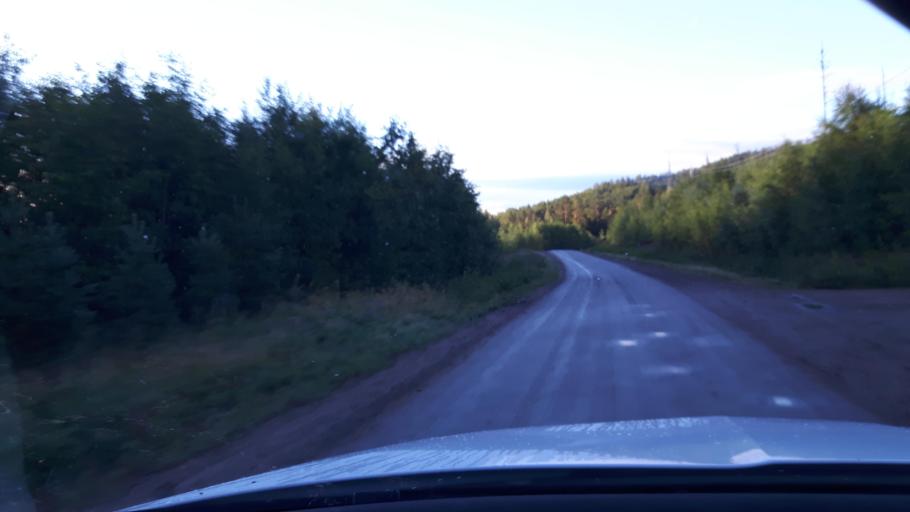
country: SE
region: Vaesternorrland
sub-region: Ange Kommun
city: Ange
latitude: 62.1705
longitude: 15.6453
